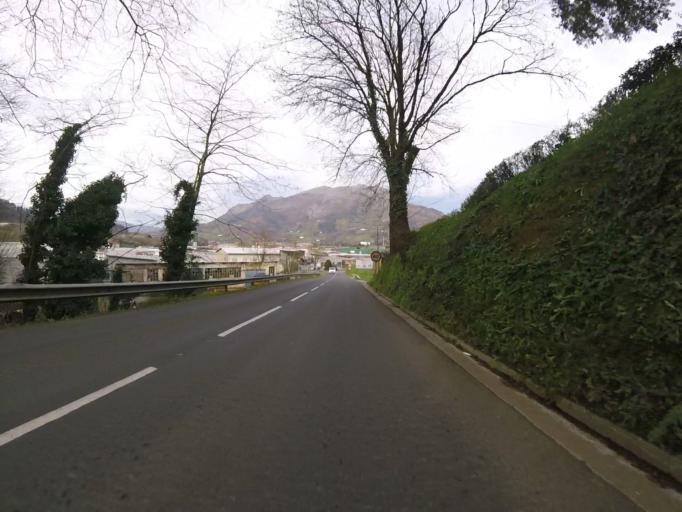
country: ES
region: Basque Country
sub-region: Provincia de Guipuzcoa
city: Azpeitia
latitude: 43.1733
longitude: -2.2505
